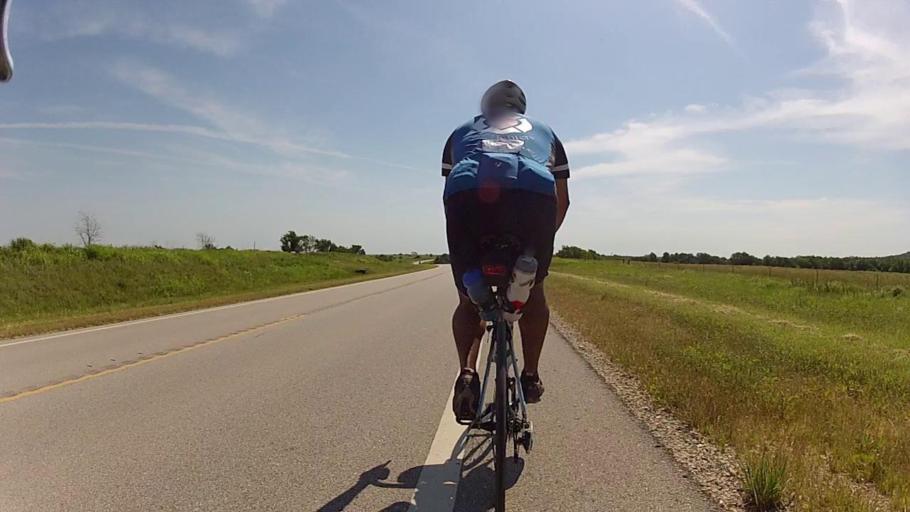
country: US
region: Kansas
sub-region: Chautauqua County
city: Sedan
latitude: 37.1070
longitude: -96.5401
